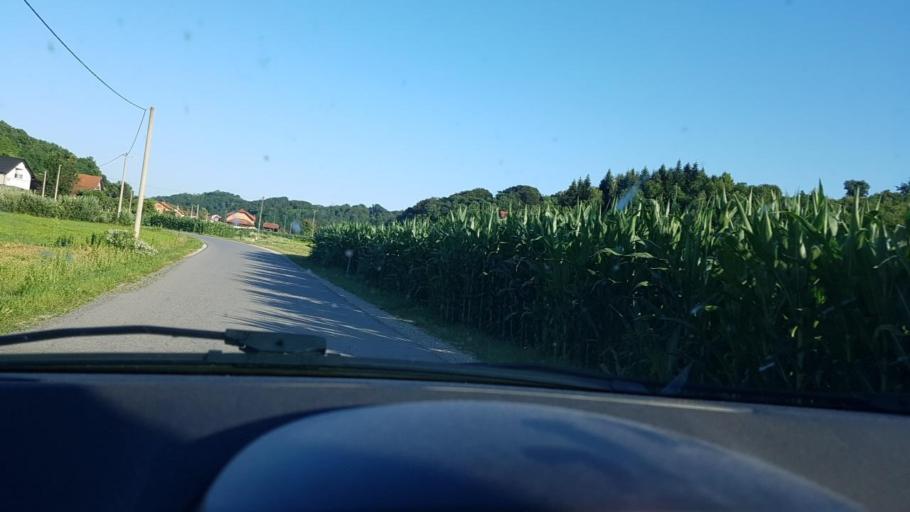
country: HR
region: Krapinsko-Zagorska
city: Mihovljan
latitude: 46.0919
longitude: 15.9585
